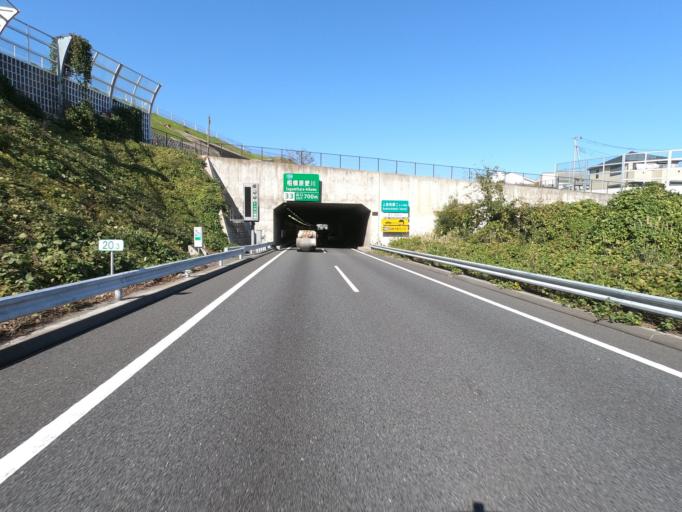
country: JP
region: Kanagawa
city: Zama
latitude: 35.5155
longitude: 139.3600
